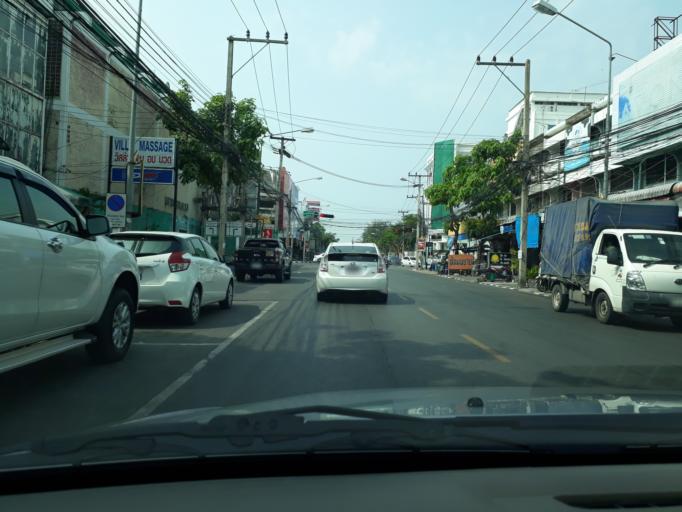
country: TH
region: Khon Kaen
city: Khon Kaen
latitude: 16.4342
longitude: 102.8363
